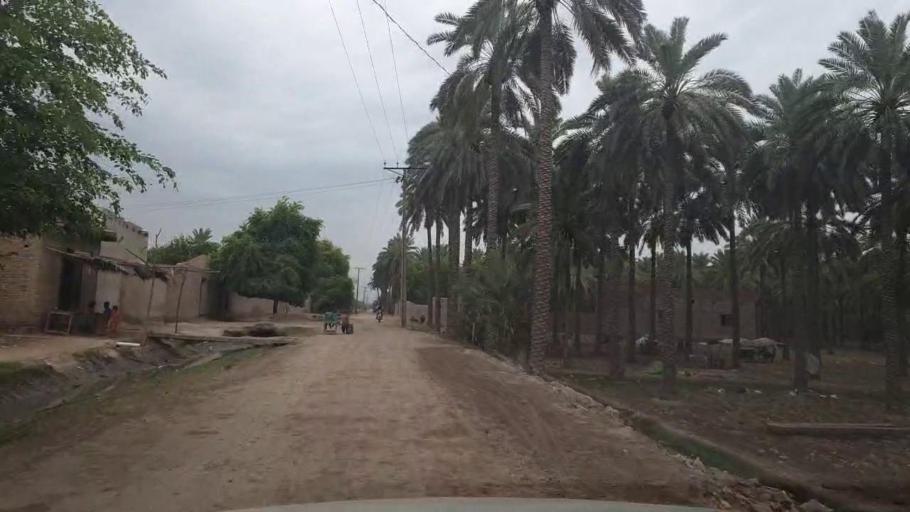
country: PK
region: Sindh
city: Sukkur
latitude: 27.6161
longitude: 68.8184
